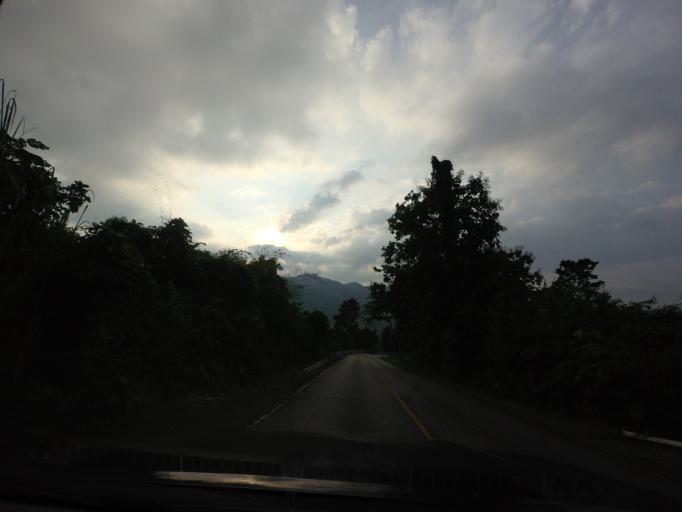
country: TH
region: Loei
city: Na Haeo
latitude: 17.3681
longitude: 101.0493
